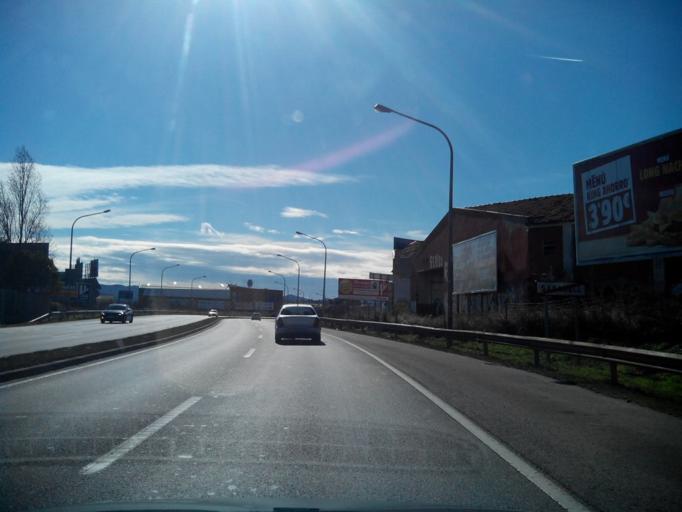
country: ES
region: Catalonia
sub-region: Provincia de Barcelona
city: Sant Quirze del Valles
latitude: 41.5379
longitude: 2.0959
